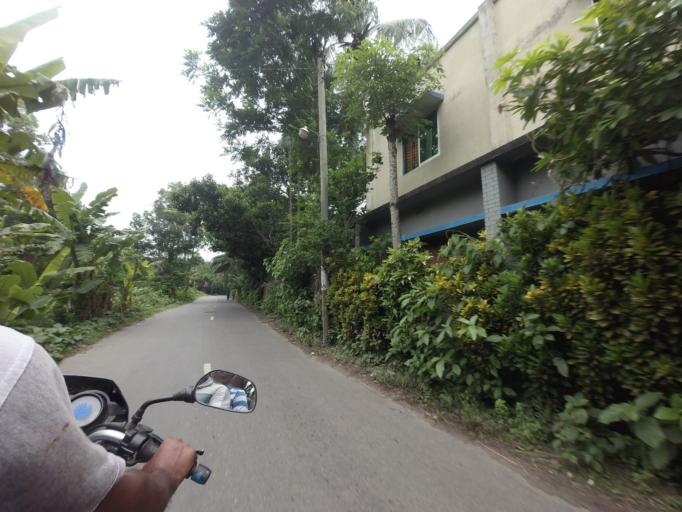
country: BD
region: Khulna
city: Kalia
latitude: 23.1668
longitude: 89.6455
